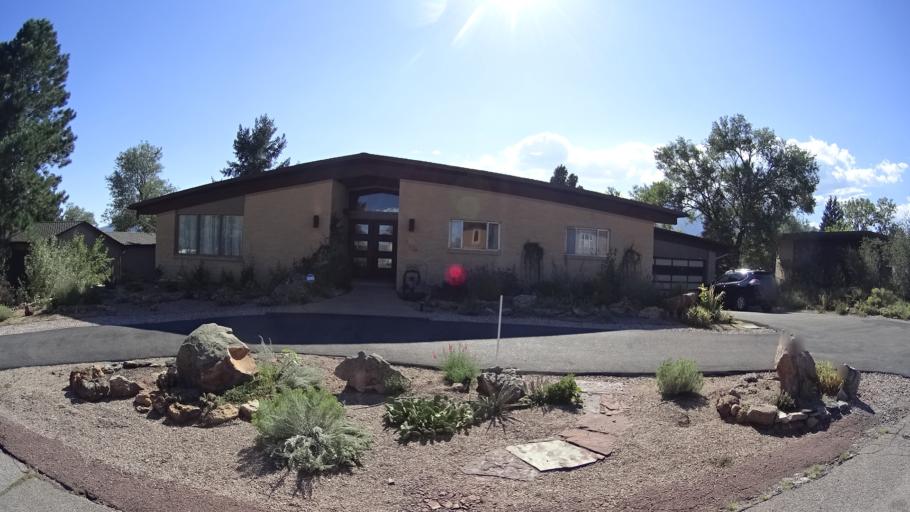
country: US
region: Colorado
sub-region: El Paso County
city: Colorado Springs
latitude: 38.8521
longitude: -104.8380
